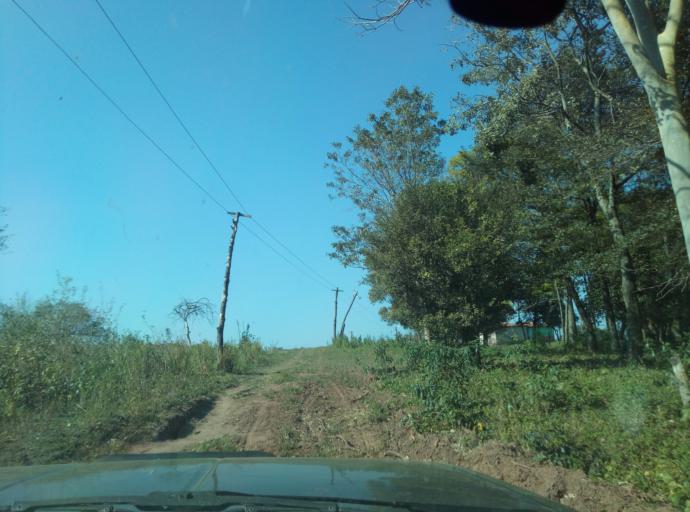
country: PY
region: Caaguazu
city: San Joaquin
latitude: -25.1762
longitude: -56.1137
